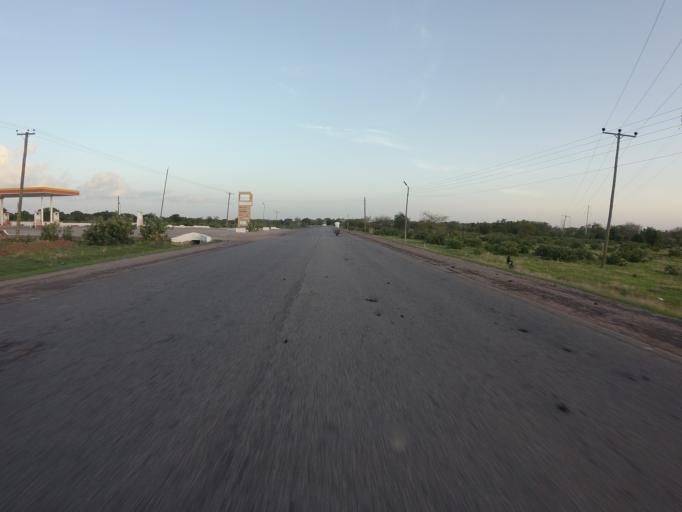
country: GH
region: Upper East
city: Navrongo
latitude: 10.9345
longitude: -1.0895
